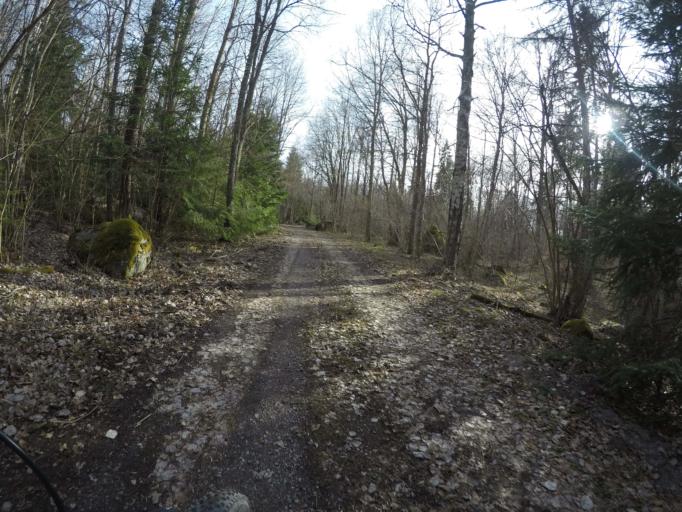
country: SE
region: Soedermanland
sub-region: Eskilstuna Kommun
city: Kvicksund
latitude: 59.4525
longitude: 16.3887
